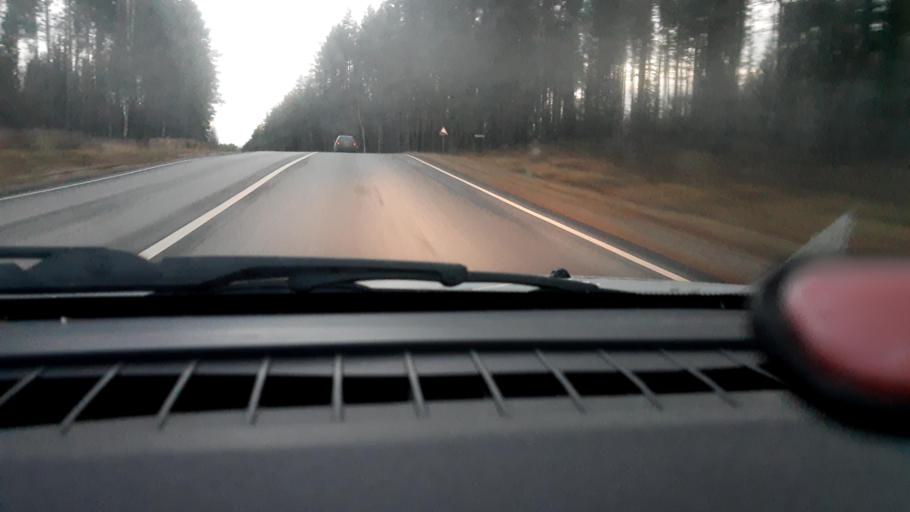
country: RU
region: Nizjnij Novgorod
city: Krasnyye Baki
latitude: 56.9933
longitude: 45.1147
